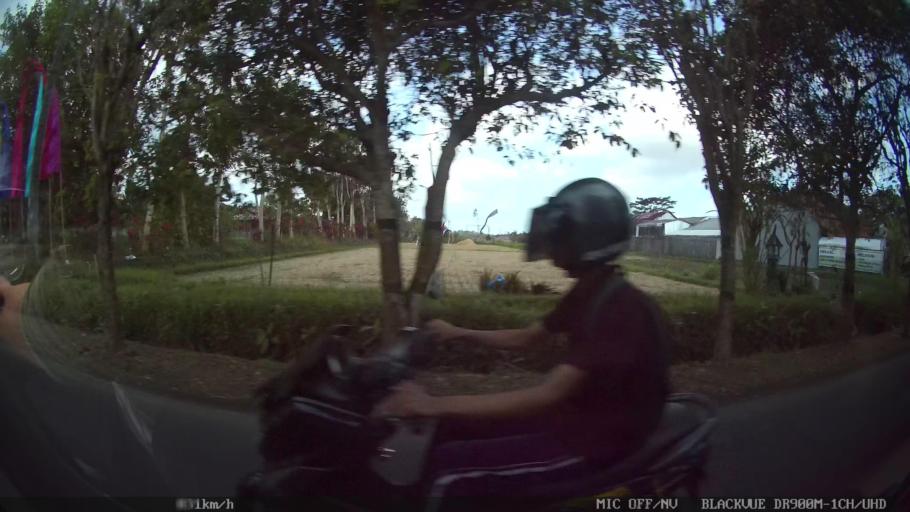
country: ID
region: Bali
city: Banjar Sedang
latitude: -8.5611
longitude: 115.2342
